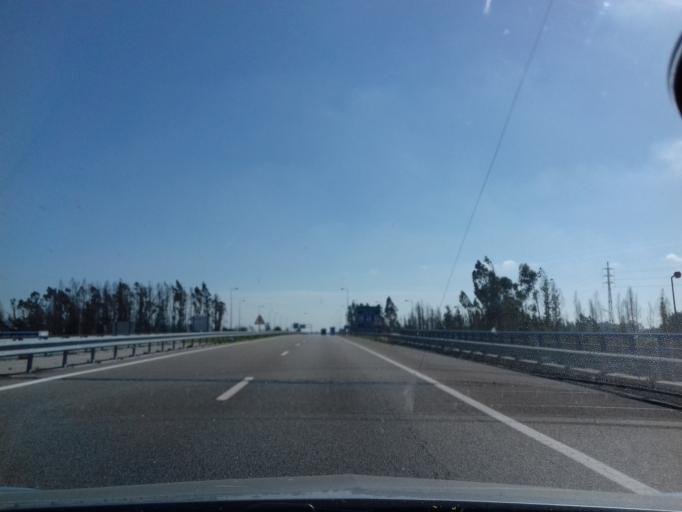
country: PT
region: Aveiro
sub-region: Aveiro
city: Oliveirinha
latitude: 40.5836
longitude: -8.6020
